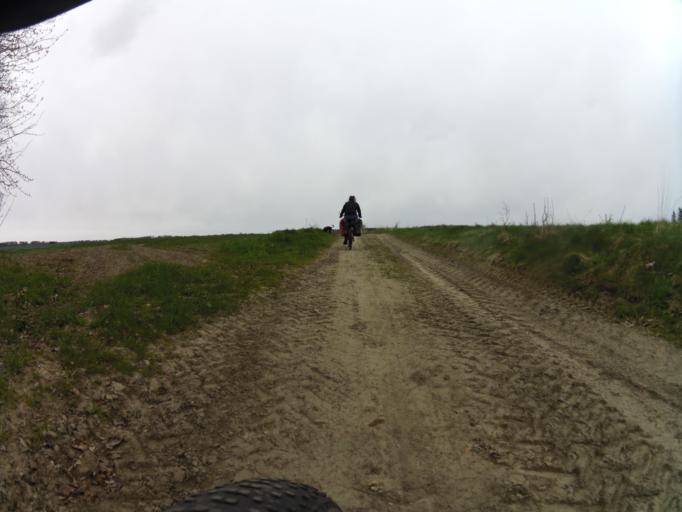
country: PL
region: West Pomeranian Voivodeship
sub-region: Powiat koszalinski
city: Polanow
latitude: 54.1042
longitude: 16.6126
